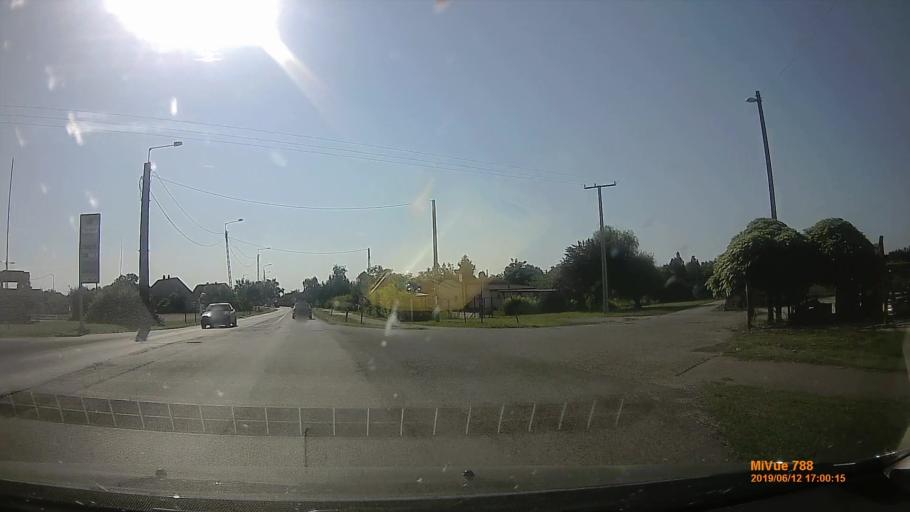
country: HU
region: Csongrad
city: Deszk
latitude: 46.2208
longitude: 20.2531
